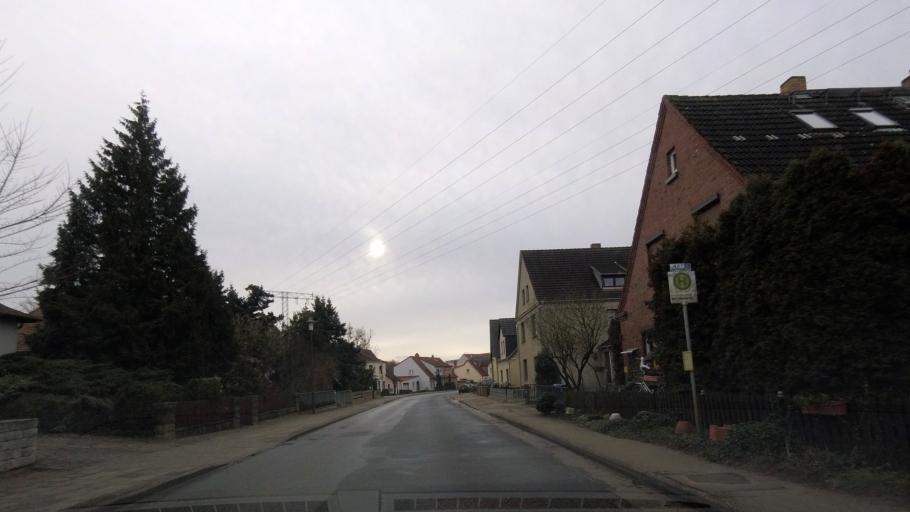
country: DE
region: Mecklenburg-Vorpommern
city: Waren
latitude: 53.5260
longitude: 12.6851
